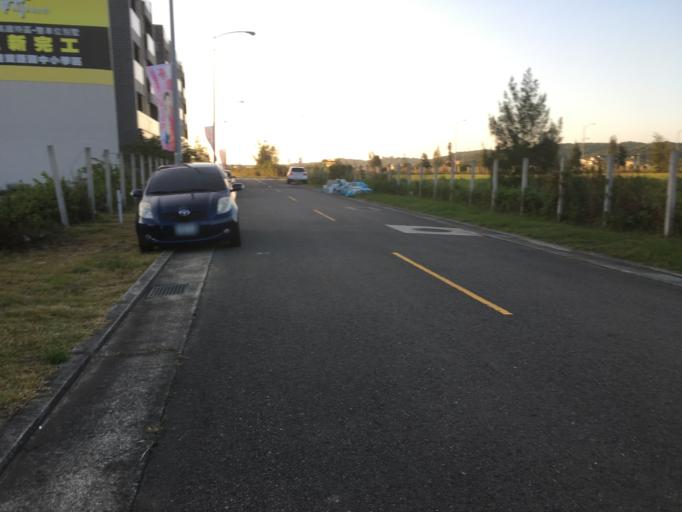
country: TW
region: Taiwan
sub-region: Miaoli
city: Miaoli
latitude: 24.6123
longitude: 120.8280
